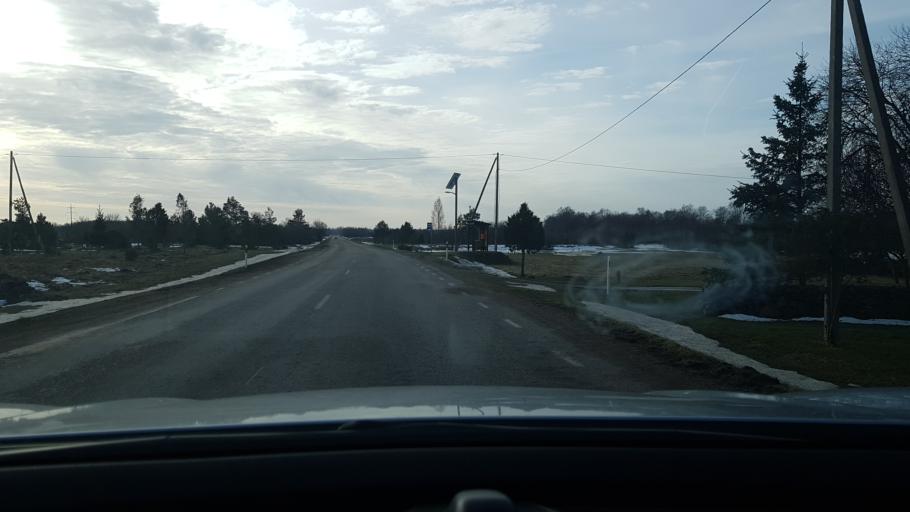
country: EE
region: Saare
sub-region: Kuressaare linn
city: Kuressaare
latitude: 58.3184
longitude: 22.5464
